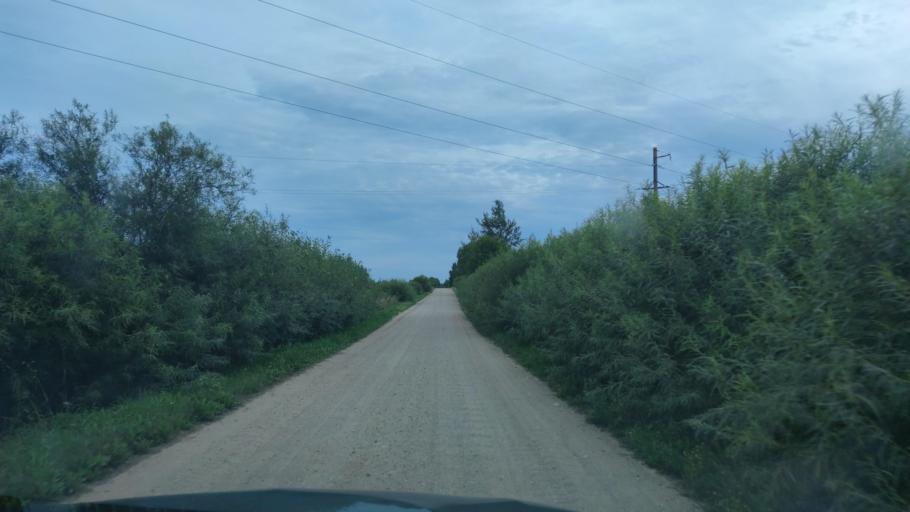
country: BY
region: Vitebsk
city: Mosar
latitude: 55.1266
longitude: 27.1581
